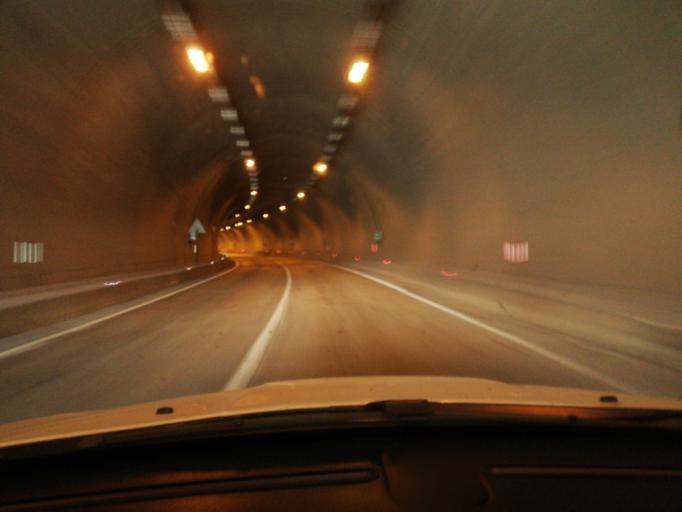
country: TR
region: Karabuk
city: Yenice
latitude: 41.1611
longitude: 32.4584
